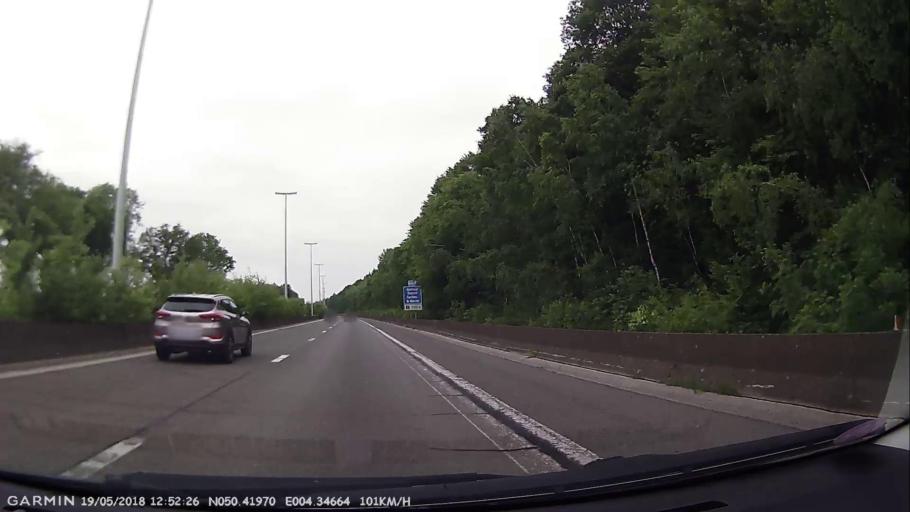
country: BE
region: Wallonia
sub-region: Province du Hainaut
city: Courcelles
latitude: 50.4200
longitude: 4.3466
